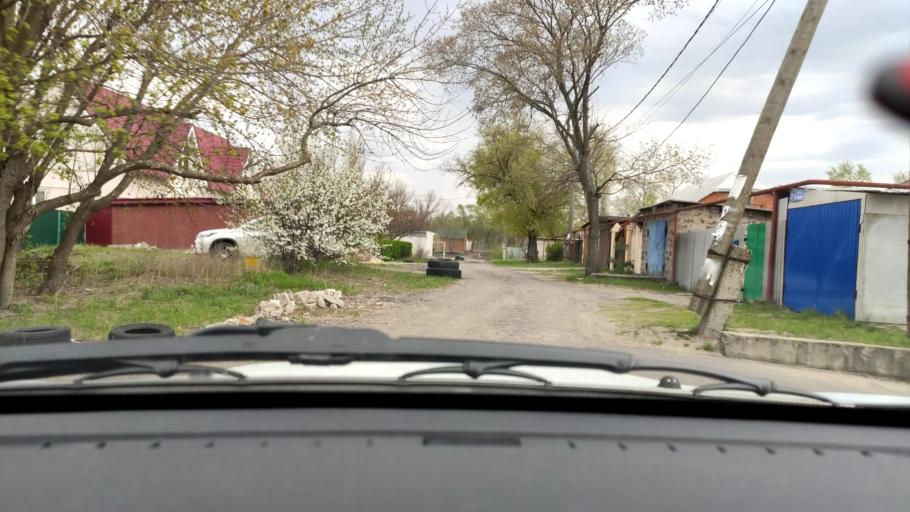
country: RU
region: Voronezj
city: Somovo
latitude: 51.7377
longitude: 39.3466
